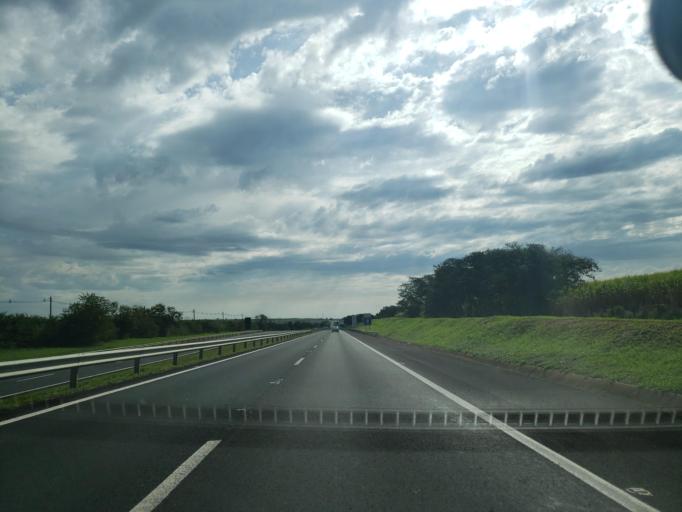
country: BR
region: Sao Paulo
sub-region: Cafelandia
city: Cafelandia
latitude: -21.8690
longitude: -49.5687
